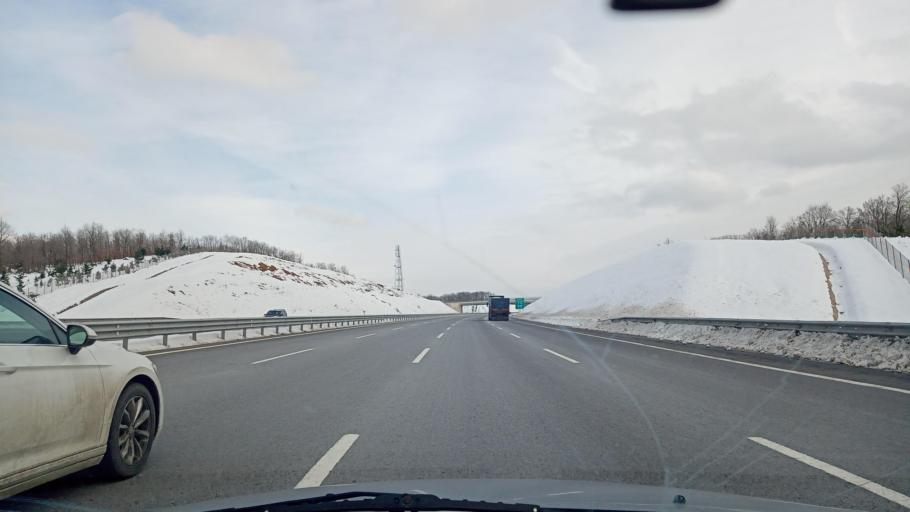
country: TR
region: Kocaeli
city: Hereke
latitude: 40.8986
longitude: 29.6378
